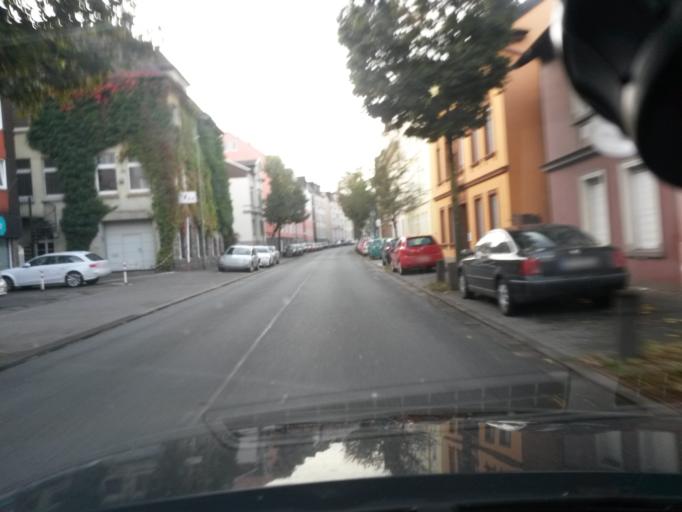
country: DE
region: North Rhine-Westphalia
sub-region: Regierungsbezirk Arnsberg
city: Luedenscheid
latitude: 51.2240
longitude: 7.6409
